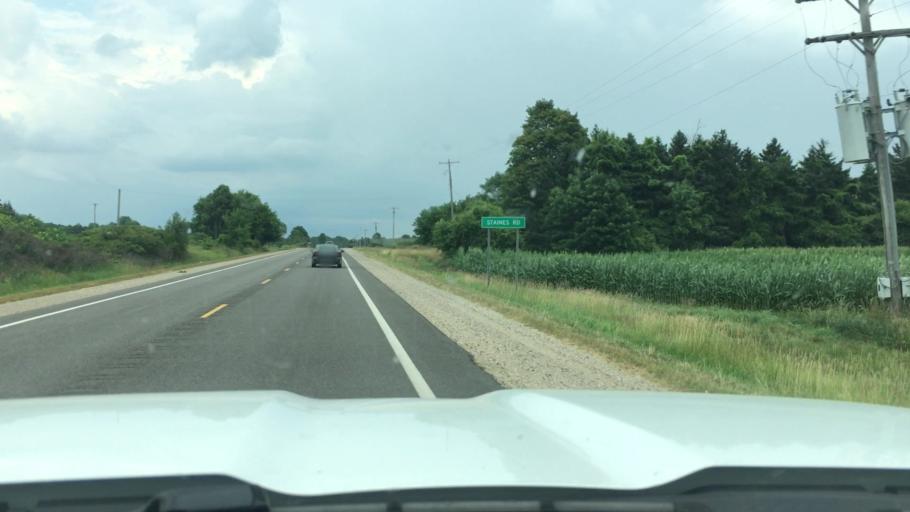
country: US
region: Michigan
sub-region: Montcalm County
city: Stanton
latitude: 43.1781
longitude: -85.0570
